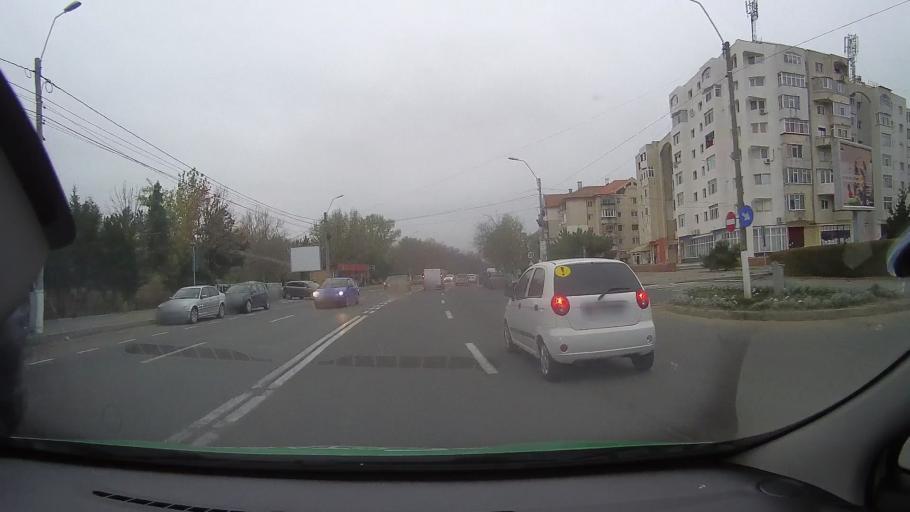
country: RO
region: Ialomita
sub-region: Comuna Slobozia
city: Slobozia
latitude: 44.5652
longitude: 27.3821
